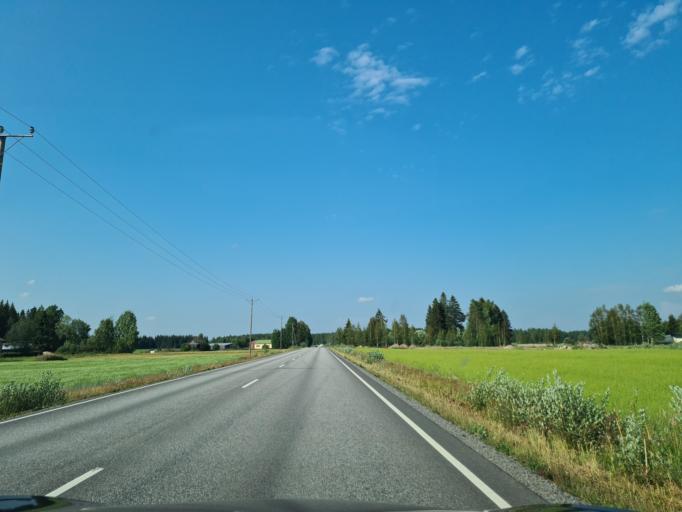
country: FI
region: Satakunta
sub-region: Pohjois-Satakunta
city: Kankaanpaeae
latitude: 61.9150
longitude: 22.5036
